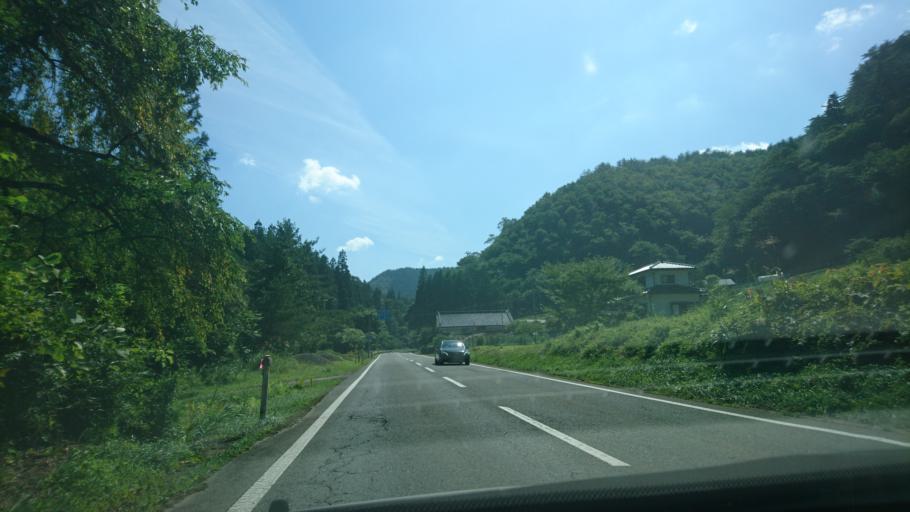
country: JP
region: Iwate
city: Ofunato
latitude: 39.0234
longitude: 141.5006
